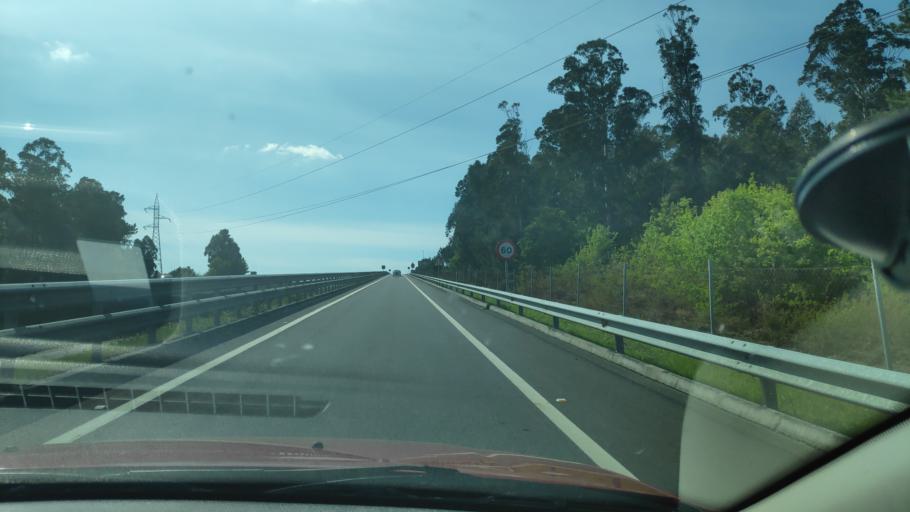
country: ES
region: Galicia
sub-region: Provincia da Coruna
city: Ames
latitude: 42.8697
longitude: -8.6540
